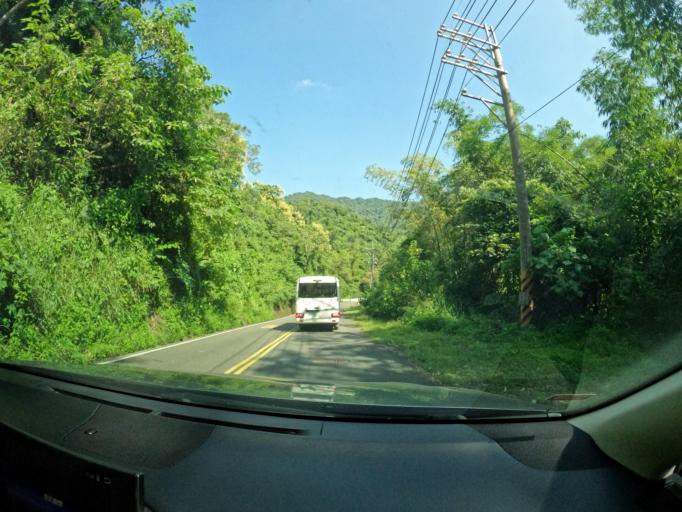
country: TW
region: Taiwan
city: Yujing
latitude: 23.0717
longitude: 120.6433
